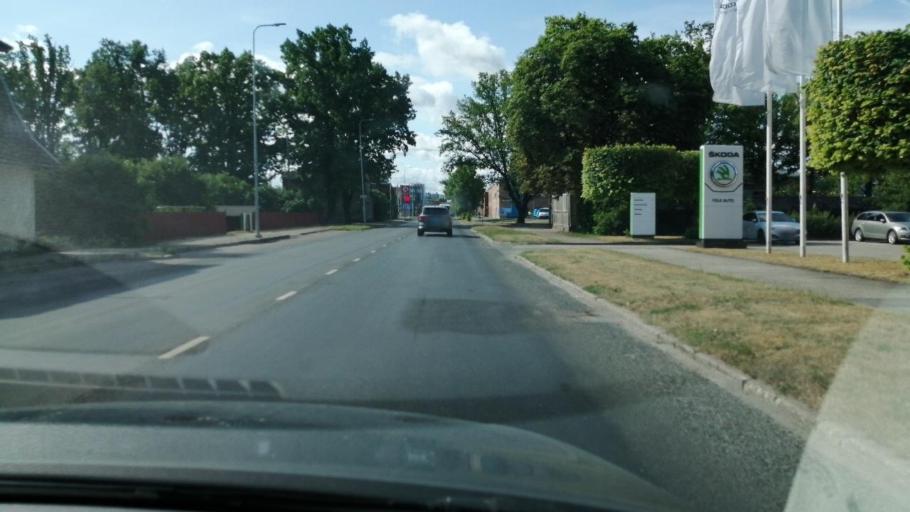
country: EE
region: Viljandimaa
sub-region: Viljandi linn
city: Viljandi
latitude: 58.3717
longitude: 25.5988
